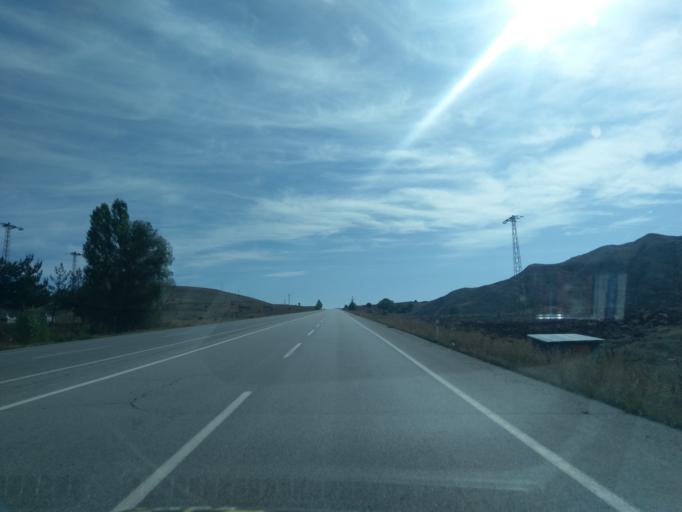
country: TR
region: Sivas
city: Imranli
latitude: 39.8845
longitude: 38.0363
